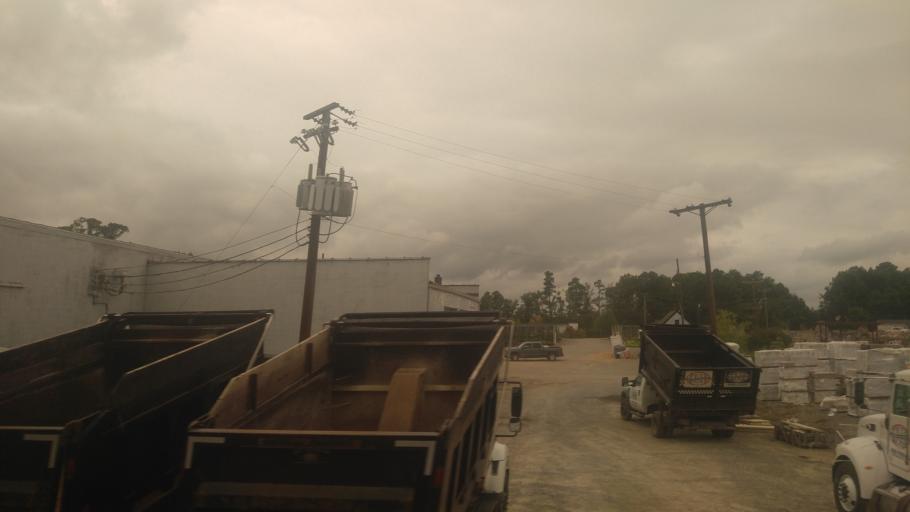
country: US
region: Virginia
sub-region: Henrico County
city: Laurel
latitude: 37.6397
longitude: -77.5065
